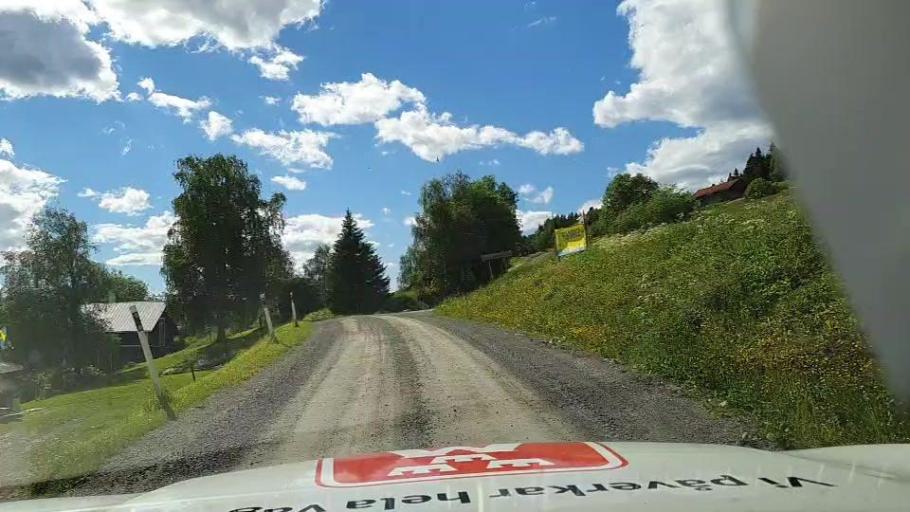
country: SE
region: Jaemtland
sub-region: Krokoms Kommun
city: Valla
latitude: 63.5688
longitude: 13.8136
